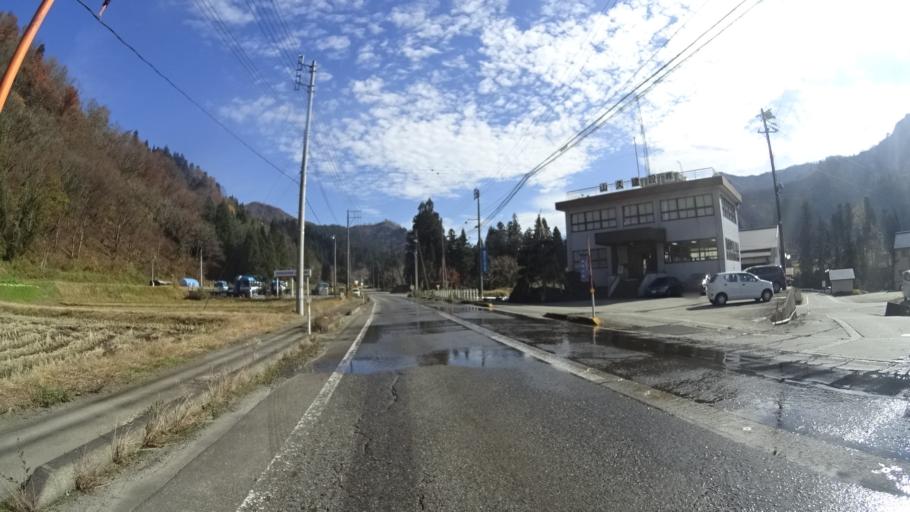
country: JP
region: Niigata
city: Muikamachi
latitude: 37.2249
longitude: 139.0162
